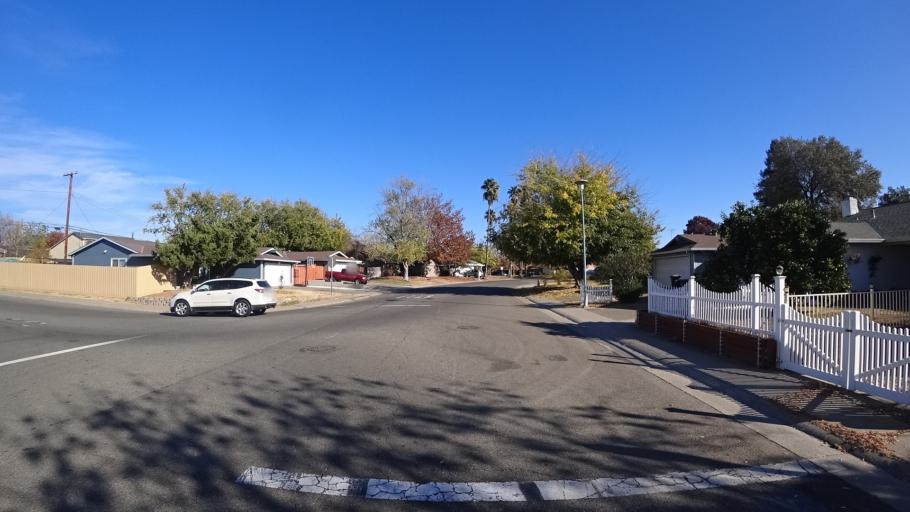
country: US
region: California
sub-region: Sacramento County
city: Antelope
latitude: 38.7142
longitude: -121.3159
